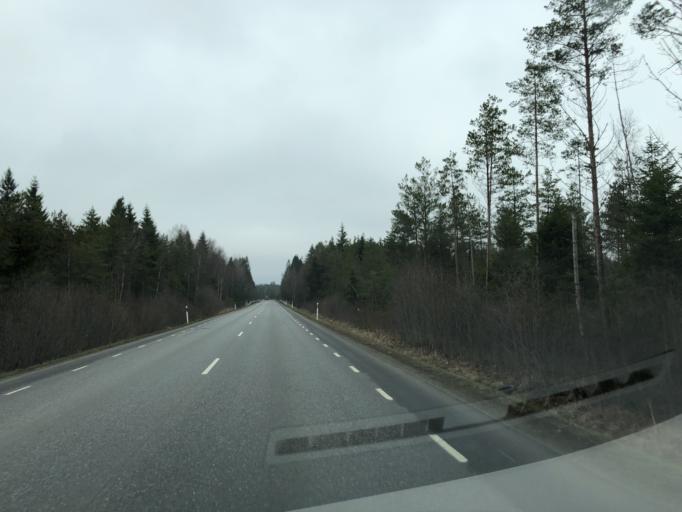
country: EE
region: Laeaene-Virumaa
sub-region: Rakke vald
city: Rakke
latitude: 59.0428
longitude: 26.2394
